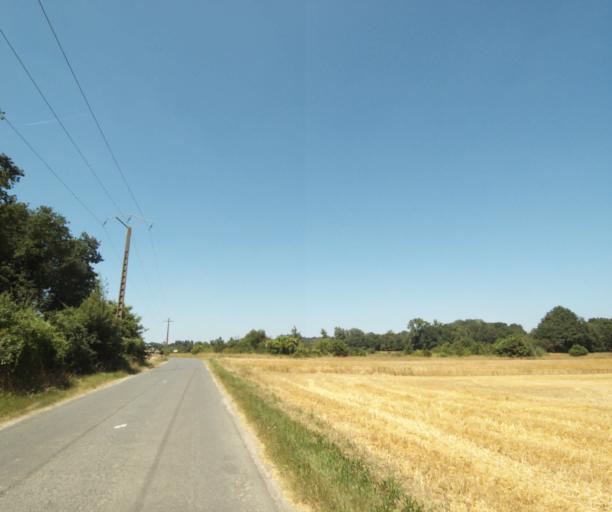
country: FR
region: Ile-de-France
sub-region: Departement de Seine-et-Marne
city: Noisy-sur-Ecole
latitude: 48.3596
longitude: 2.5133
